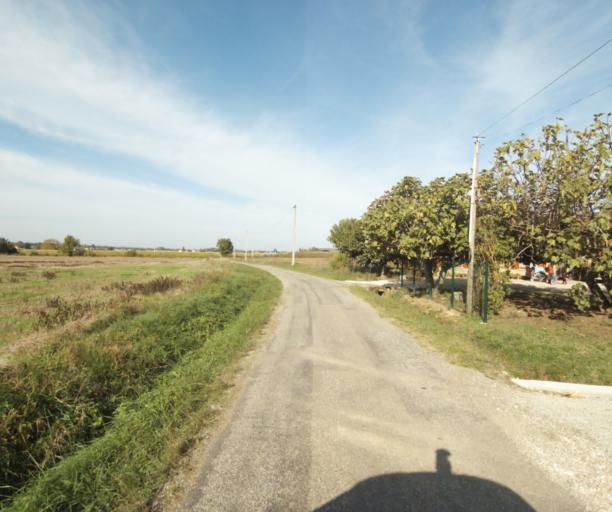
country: FR
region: Midi-Pyrenees
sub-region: Departement du Tarn-et-Garonne
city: Nohic
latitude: 43.9140
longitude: 1.4371
